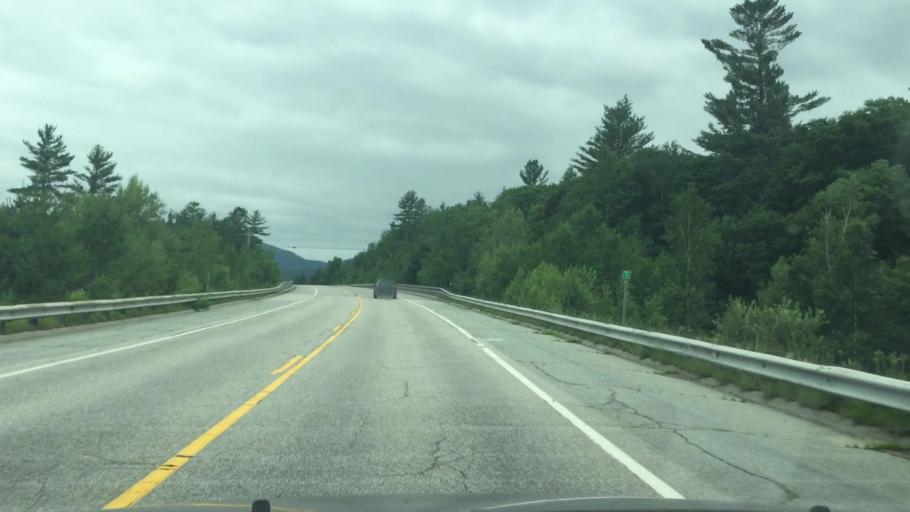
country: US
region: New Hampshire
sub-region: Carroll County
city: North Conway
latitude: 44.1145
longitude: -71.3541
